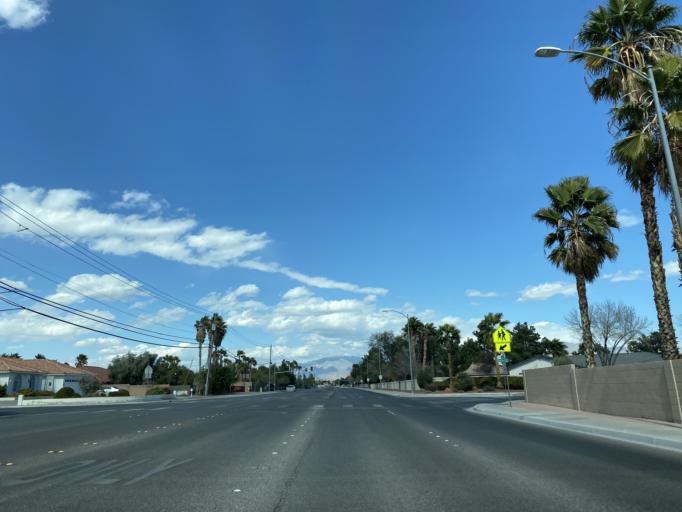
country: US
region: Nevada
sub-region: Clark County
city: Spring Valley
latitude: 36.2437
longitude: -115.2603
